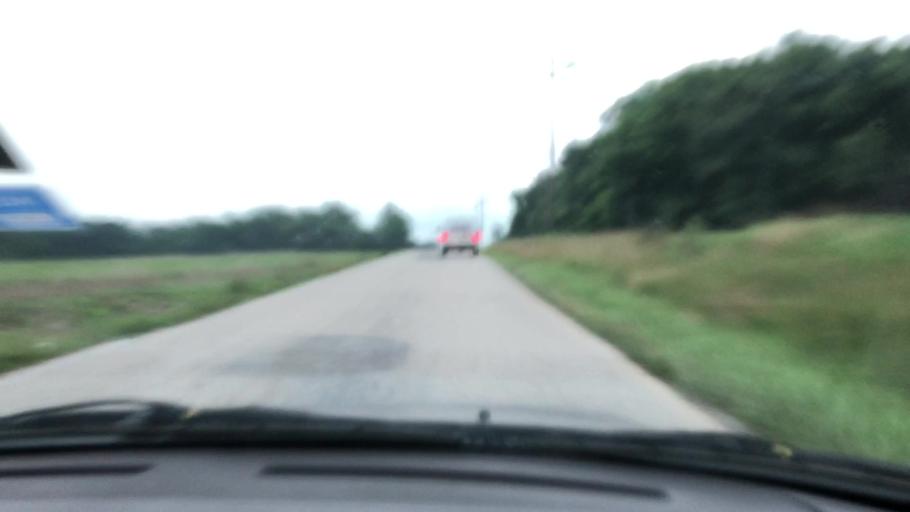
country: US
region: Indiana
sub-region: Greene County
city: Linton
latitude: 38.9805
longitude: -87.2981
